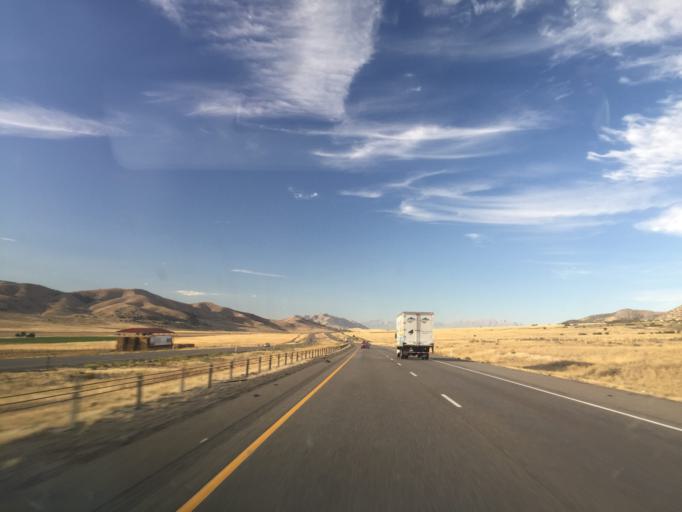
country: US
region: Utah
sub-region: Juab County
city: Mona
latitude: 39.8768
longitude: -111.8283
